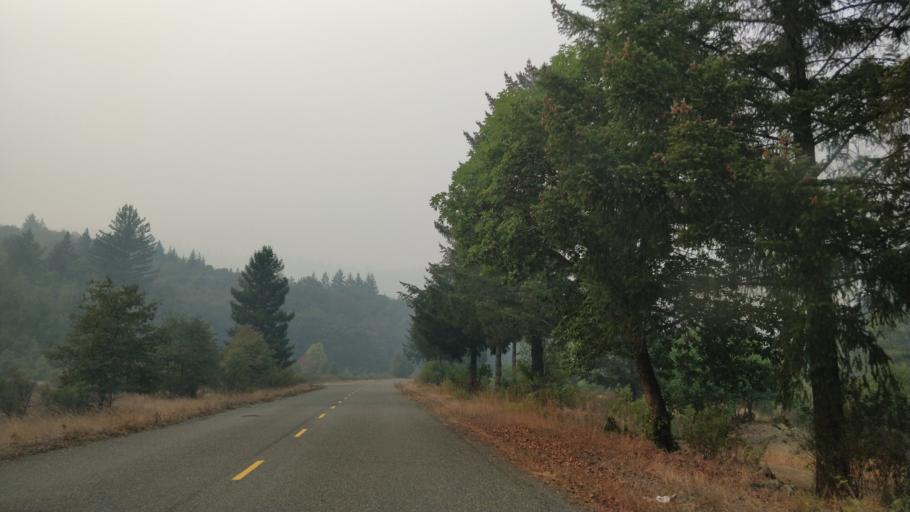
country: US
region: California
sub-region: Humboldt County
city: Rio Dell
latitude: 40.3353
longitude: -124.0263
